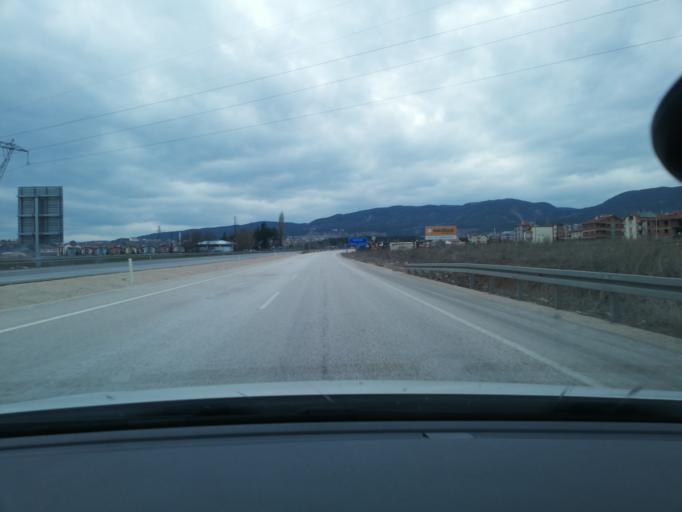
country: TR
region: Bolu
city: Gerede
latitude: 40.7819
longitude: 32.2134
